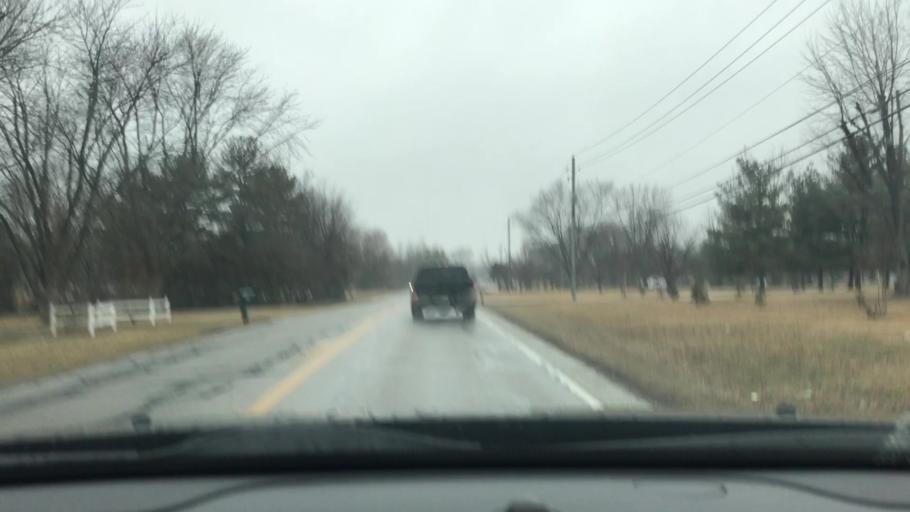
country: US
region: Indiana
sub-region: Morgan County
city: Mooresville
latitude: 39.5869
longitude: -86.3294
